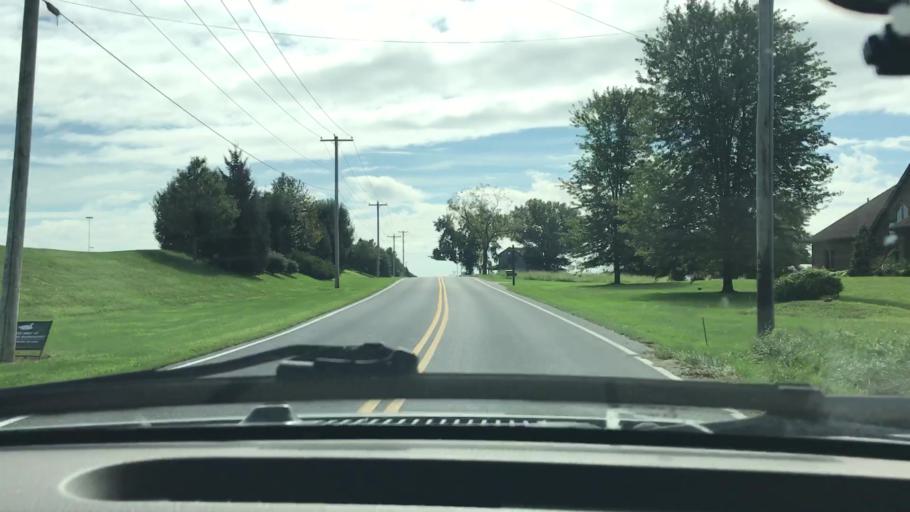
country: US
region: Pennsylvania
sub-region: Lancaster County
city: Manheim
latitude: 40.1404
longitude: -76.4069
